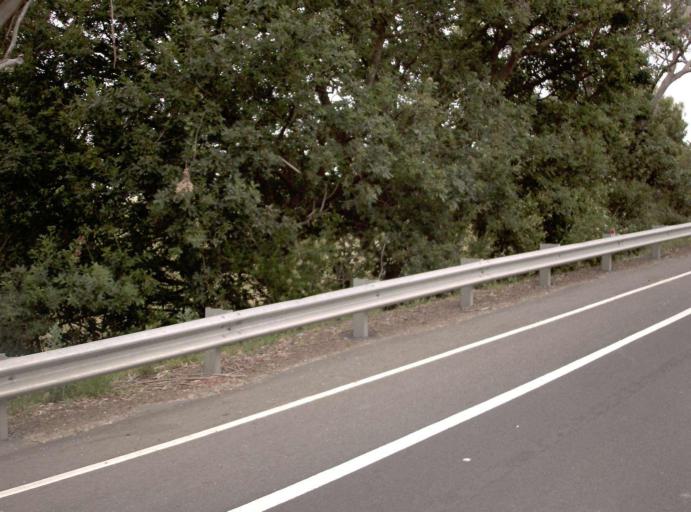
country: AU
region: Victoria
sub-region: Mornington Peninsula
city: Mount Martha
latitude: -38.2650
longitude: 145.0373
